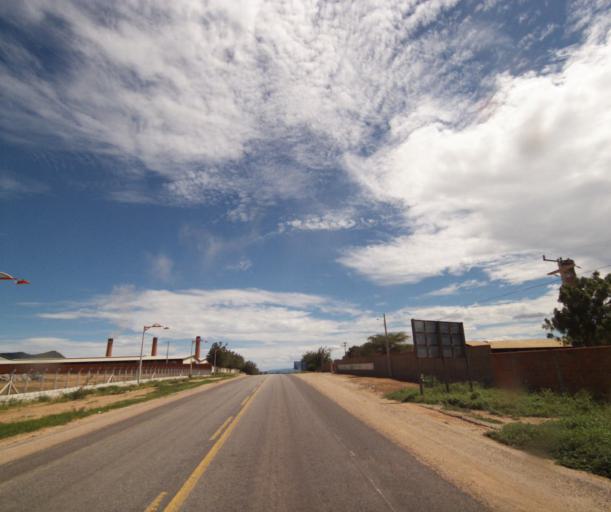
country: BR
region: Bahia
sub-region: Guanambi
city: Guanambi
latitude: -14.2618
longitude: -42.7825
